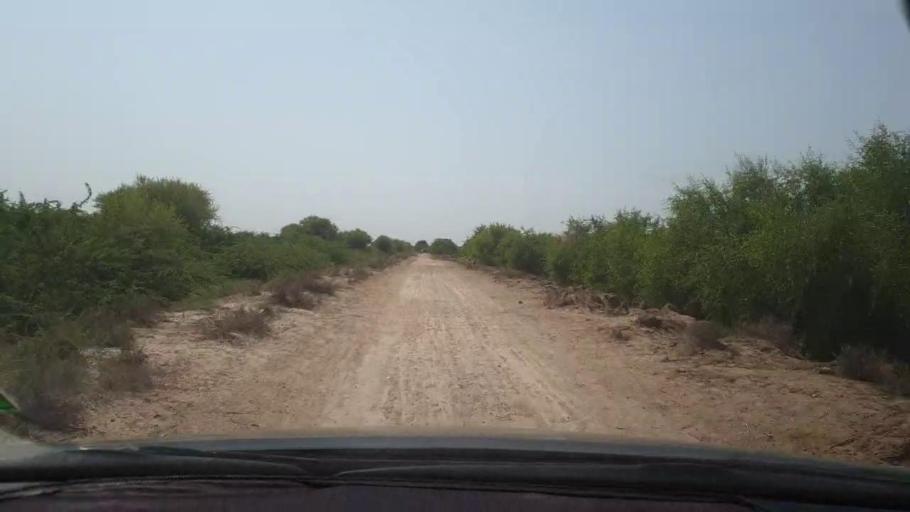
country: PK
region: Sindh
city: Tando Bago
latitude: 24.7880
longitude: 69.1767
